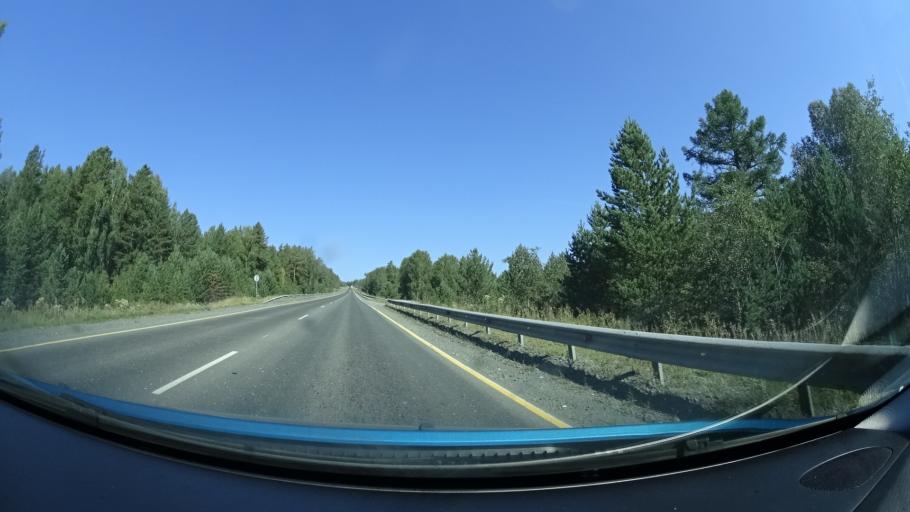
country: RU
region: Bashkortostan
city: Abzakovo
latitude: 53.8761
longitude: 58.5341
